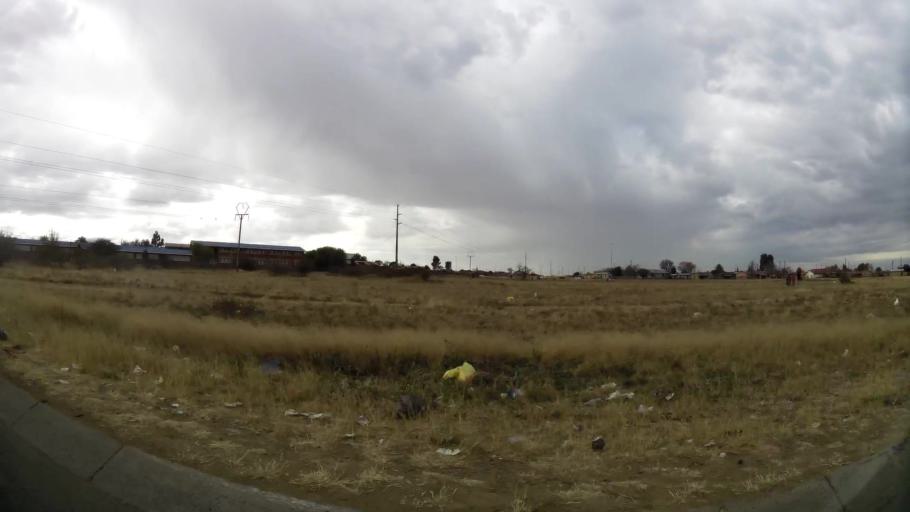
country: ZA
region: Orange Free State
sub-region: Fezile Dabi District Municipality
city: Kroonstad
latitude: -27.6562
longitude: 27.1998
